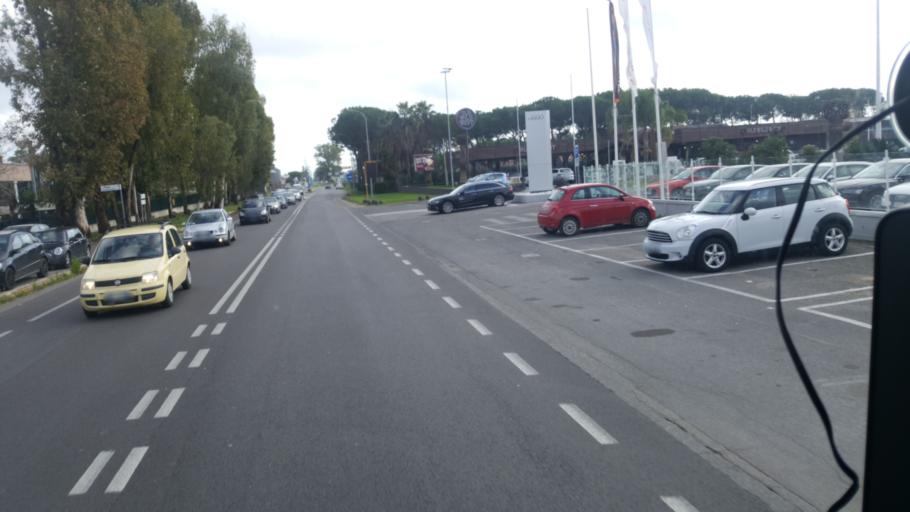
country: IT
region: Latium
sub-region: Provincia di Latina
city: Latina
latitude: 41.4800
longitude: 12.8692
